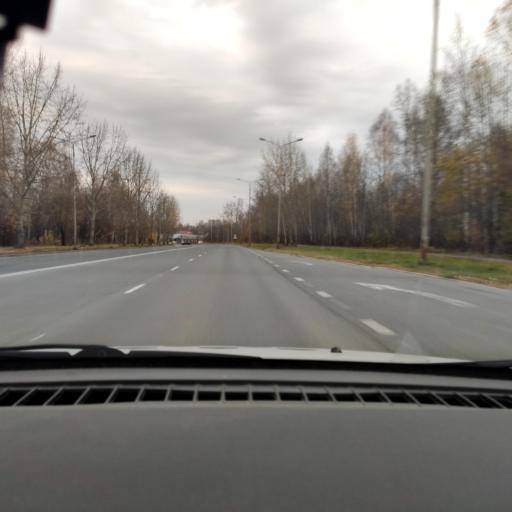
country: RU
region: Perm
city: Perm
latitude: 58.1095
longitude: 56.3979
